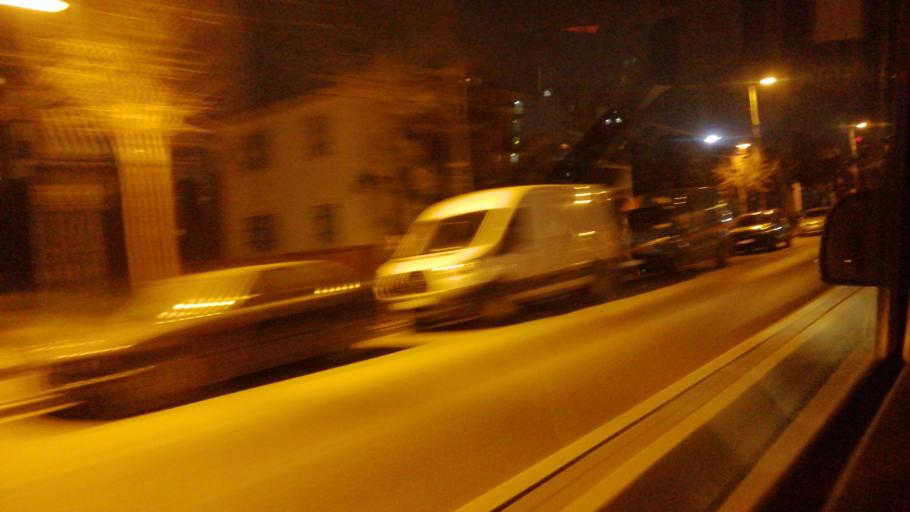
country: TR
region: Istanbul
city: Umraniye
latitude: 41.0147
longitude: 29.1285
